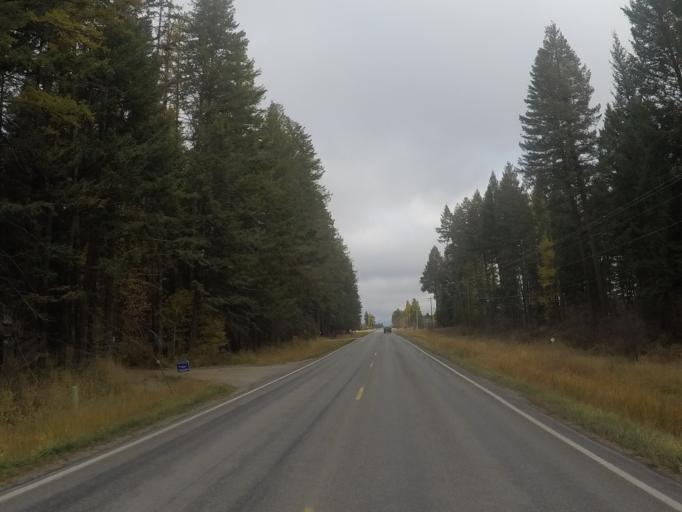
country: US
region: Montana
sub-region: Flathead County
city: Columbia Falls
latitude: 48.3137
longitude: -114.1594
